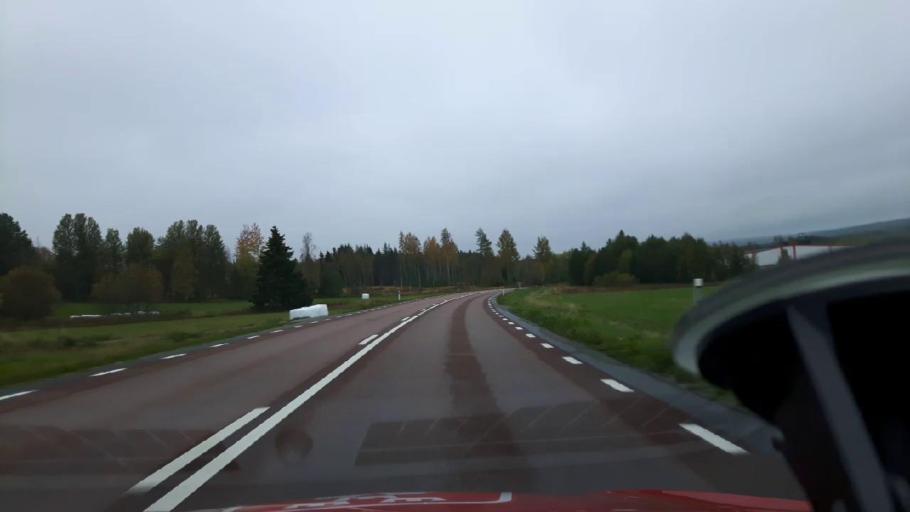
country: SE
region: Jaemtland
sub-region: Bergs Kommun
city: Hoverberg
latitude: 62.7597
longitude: 14.4380
